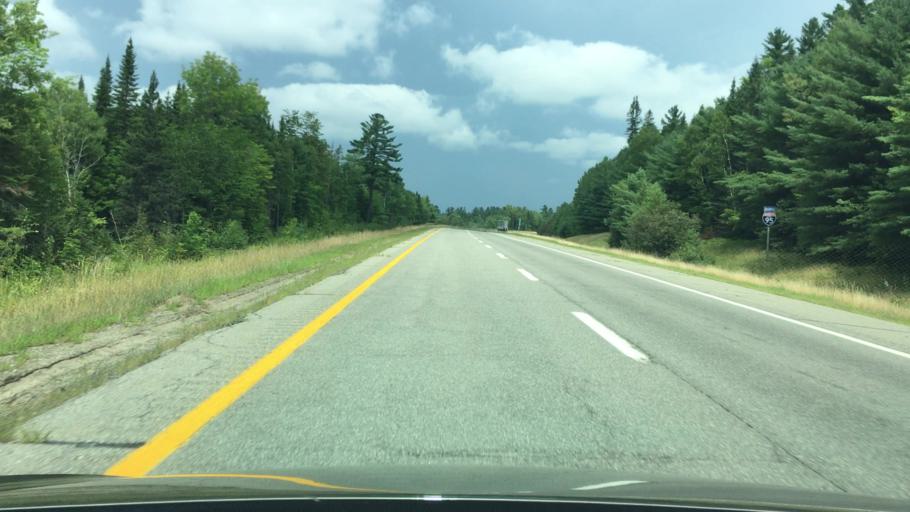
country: US
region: Maine
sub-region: Penobscot County
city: Lincoln
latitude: 45.3826
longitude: -68.6045
